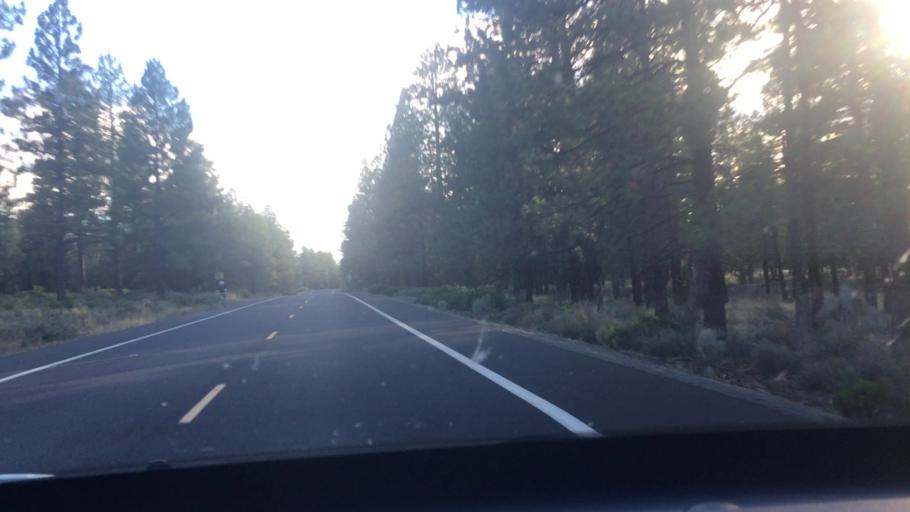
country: US
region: Oregon
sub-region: Deschutes County
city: Deschutes River Woods
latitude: 44.0456
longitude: -121.4008
